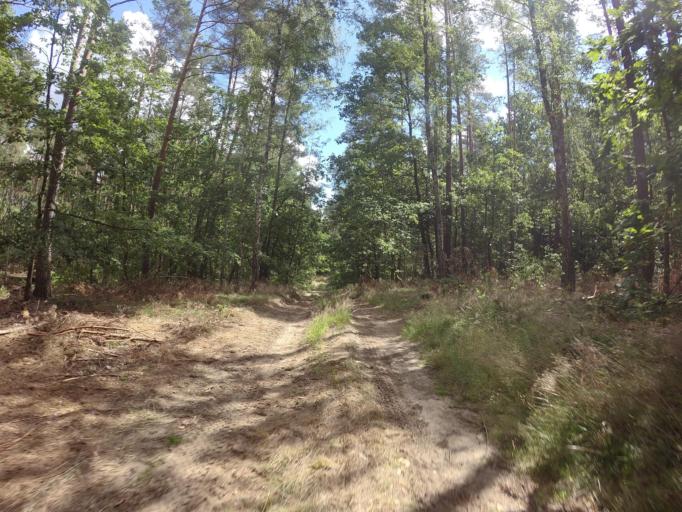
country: PL
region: West Pomeranian Voivodeship
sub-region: Powiat choszczenski
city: Drawno
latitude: 53.2952
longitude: 15.7497
